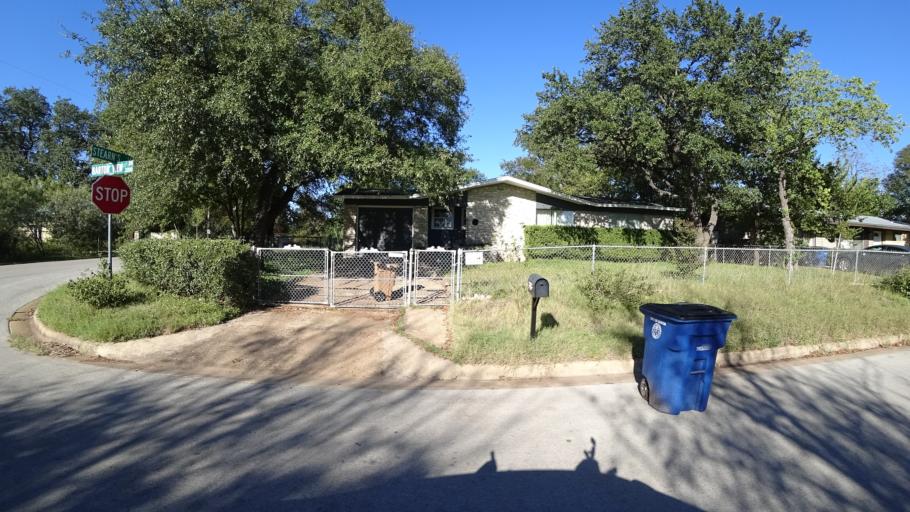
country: US
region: Texas
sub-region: Travis County
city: Rollingwood
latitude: 30.2351
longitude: -97.8103
